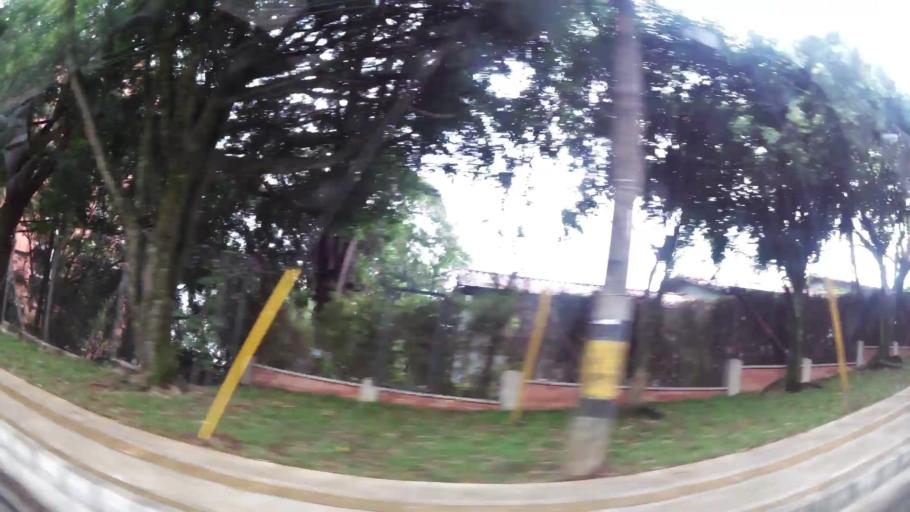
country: CO
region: Antioquia
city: Envigado
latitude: 6.1834
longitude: -75.5638
